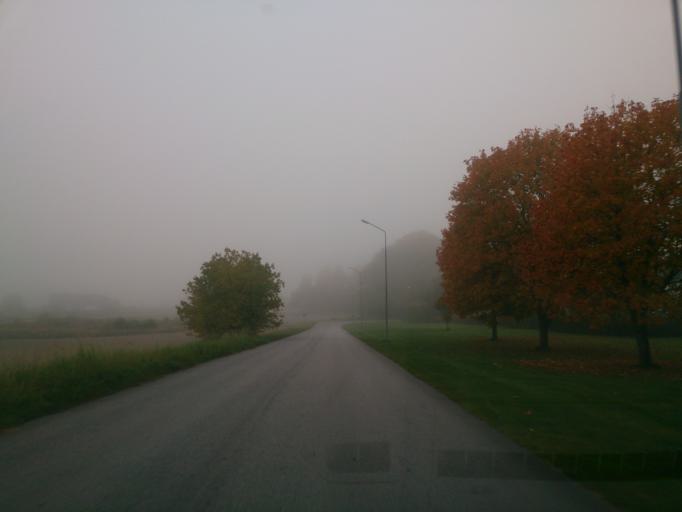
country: SE
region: OEstergoetland
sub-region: Kinda Kommun
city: Rimforsa
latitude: 58.1343
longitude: 15.6768
